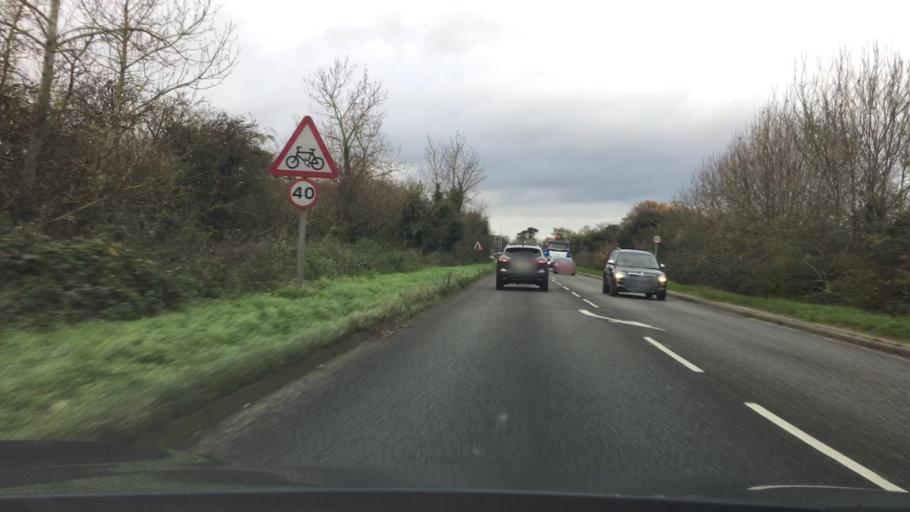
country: GB
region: England
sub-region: Nottinghamshire
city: Lowdham
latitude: 52.9912
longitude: -0.9903
